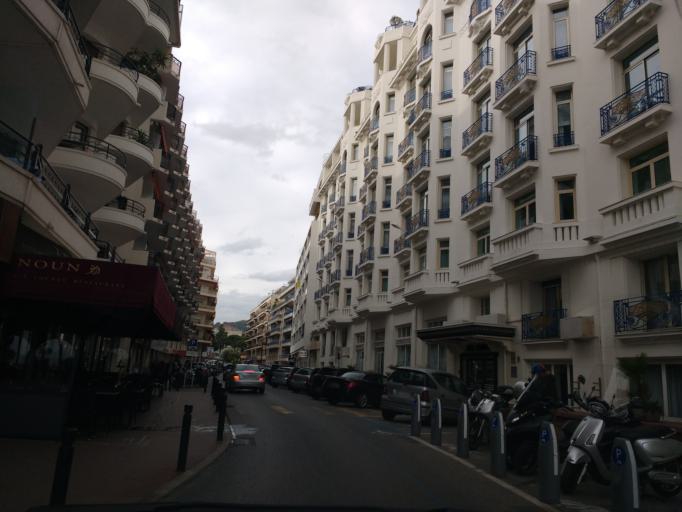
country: FR
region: Provence-Alpes-Cote d'Azur
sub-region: Departement des Alpes-Maritimes
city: Cannes
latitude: 43.5483
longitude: 7.0304
